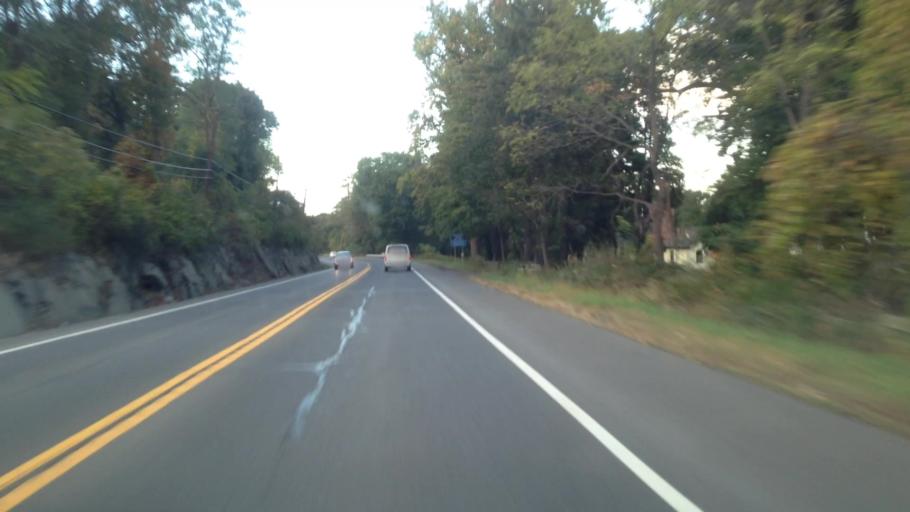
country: US
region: New York
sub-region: Dutchess County
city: Hyde Park
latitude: 41.7833
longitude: -73.9597
